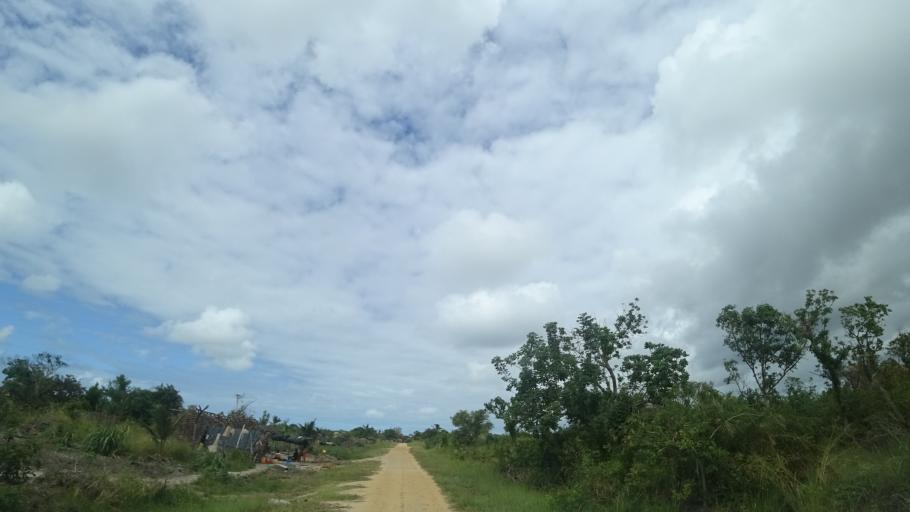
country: MZ
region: Sofala
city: Beira
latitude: -19.6128
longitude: 35.2147
